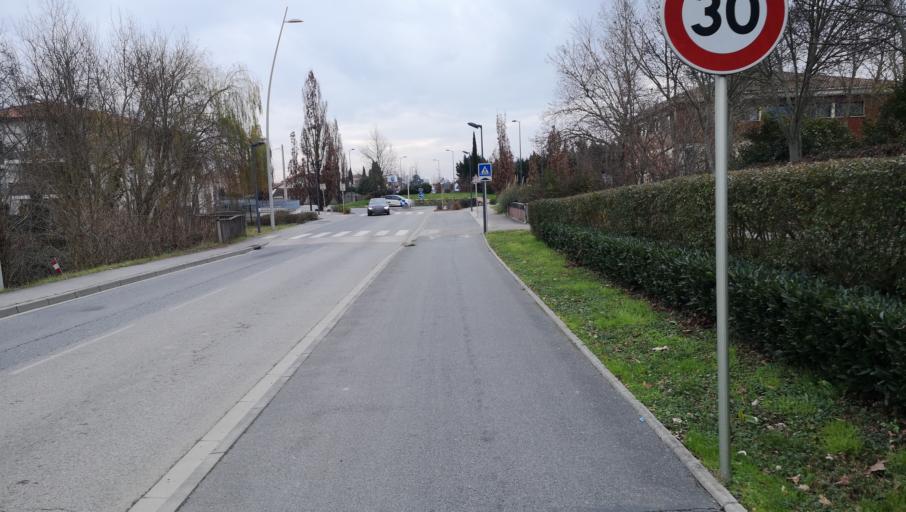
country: FR
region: Midi-Pyrenees
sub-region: Departement de la Haute-Garonne
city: Beauzelle
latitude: 43.6510
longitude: 1.3811
